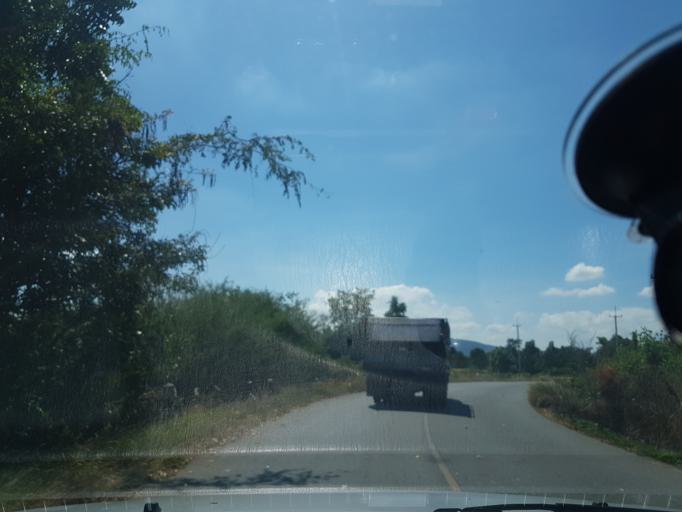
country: TH
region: Lop Buri
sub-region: Amphoe Tha Luang
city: Tha Luang
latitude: 14.9898
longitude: 101.0109
